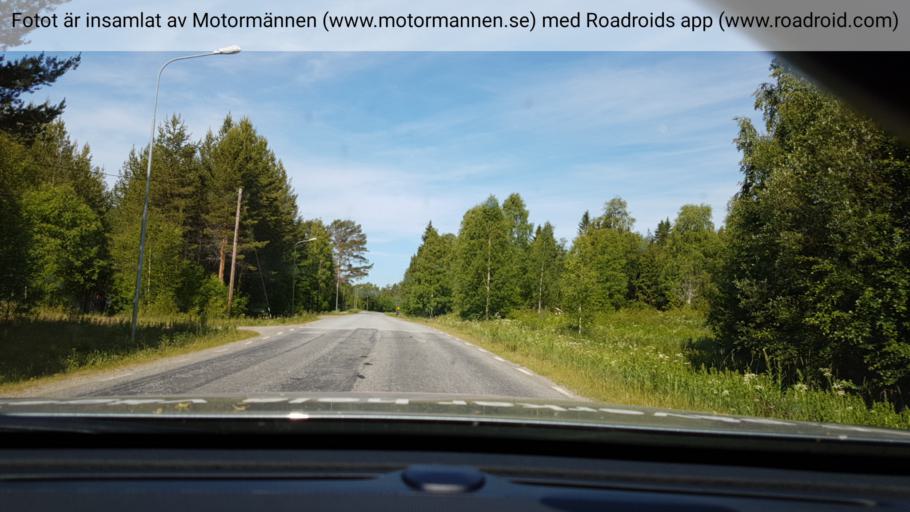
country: SE
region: Vaesterbotten
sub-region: Dorotea Kommun
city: Dorotea
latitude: 64.3396
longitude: 16.2688
